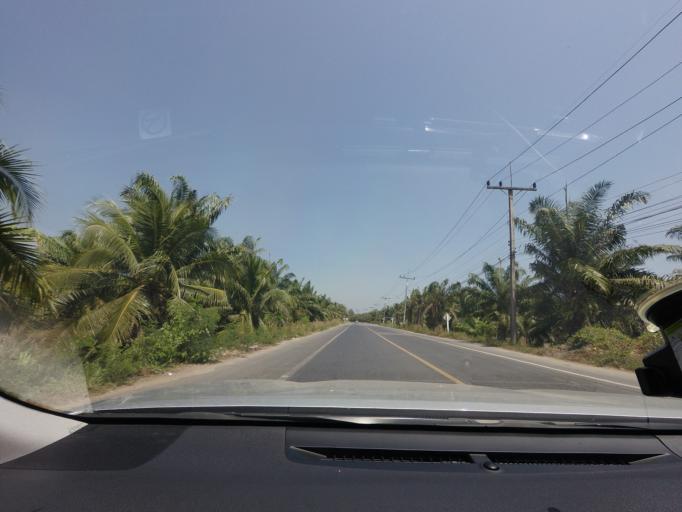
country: TH
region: Surat Thani
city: Tha Chang
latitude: 9.1974
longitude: 99.2465
